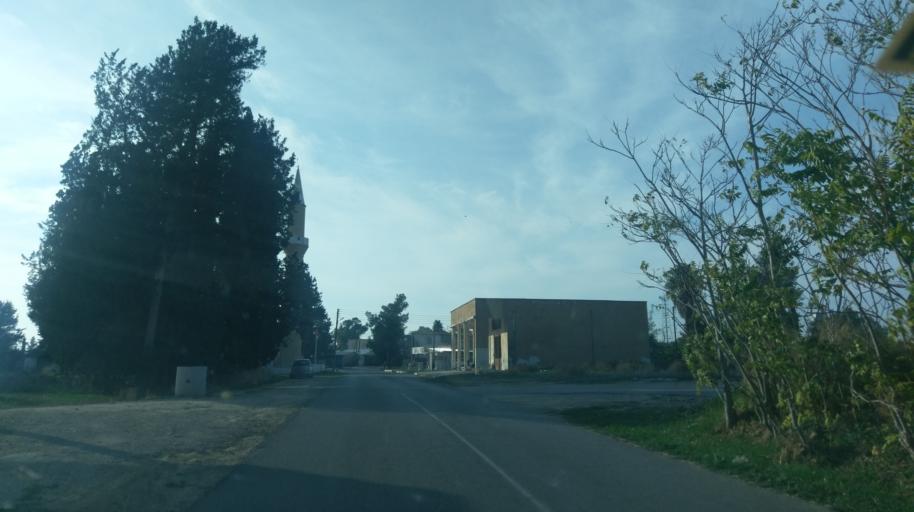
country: CY
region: Ammochostos
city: Achna
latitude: 35.1078
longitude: 33.7540
